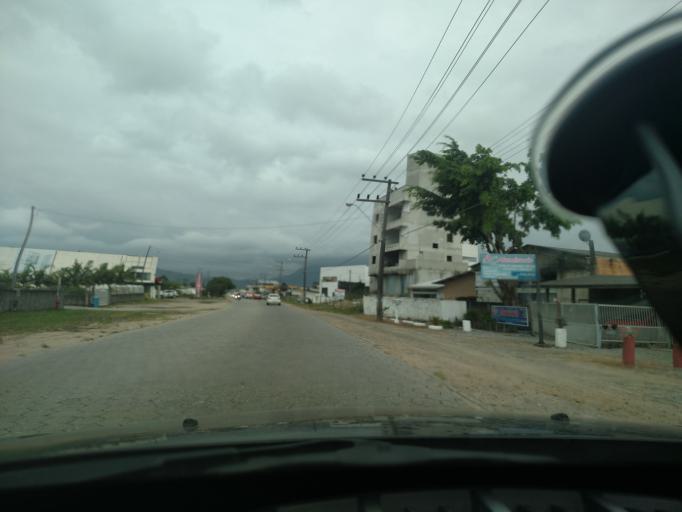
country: BR
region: Santa Catarina
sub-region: Porto Belo
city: Porto Belo
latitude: -27.1569
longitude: -48.5885
